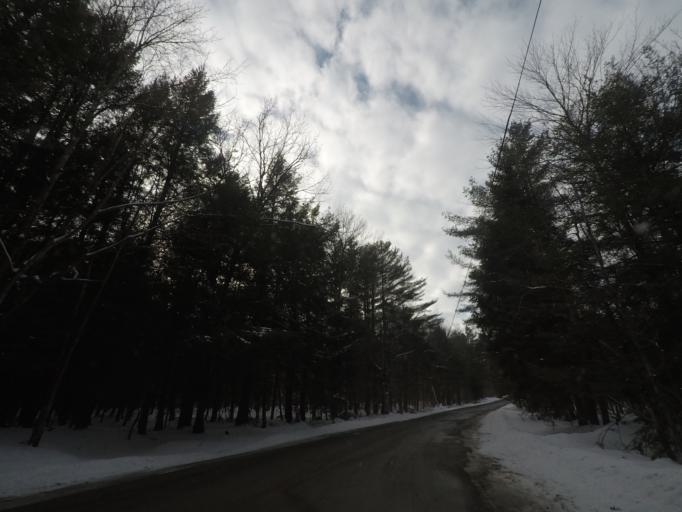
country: US
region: New York
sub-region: Rensselaer County
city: Averill Park
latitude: 42.6345
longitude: -73.4821
